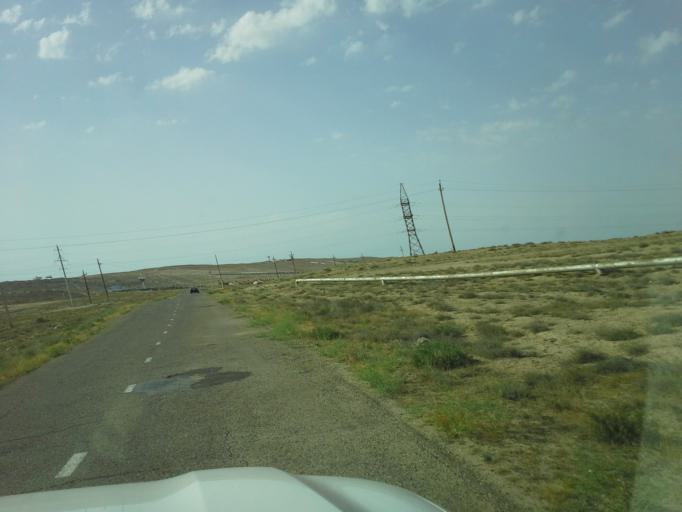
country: TM
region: Balkan
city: Turkmenbasy
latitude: 40.0339
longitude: 52.9781
